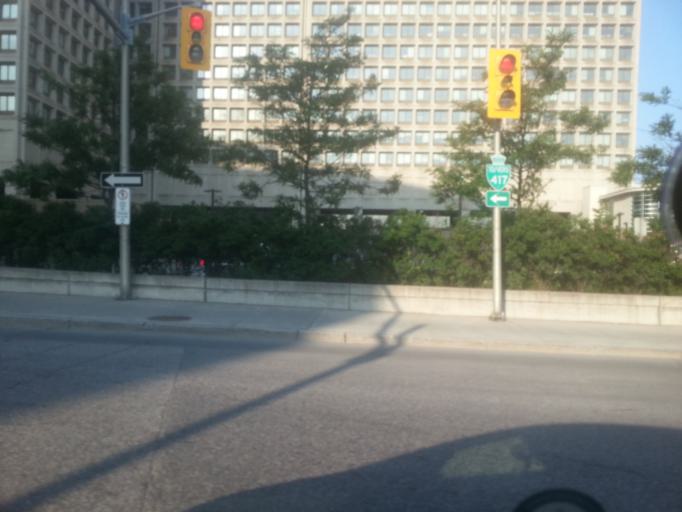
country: CA
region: Ontario
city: Ottawa
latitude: 45.4242
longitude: -75.6883
